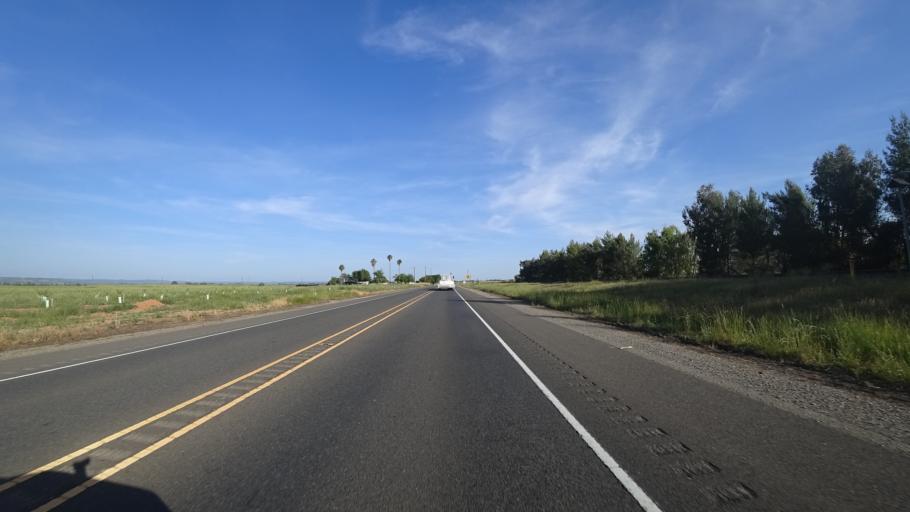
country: US
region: California
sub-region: Placer County
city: Sheridan
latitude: 38.9647
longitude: -121.3628
